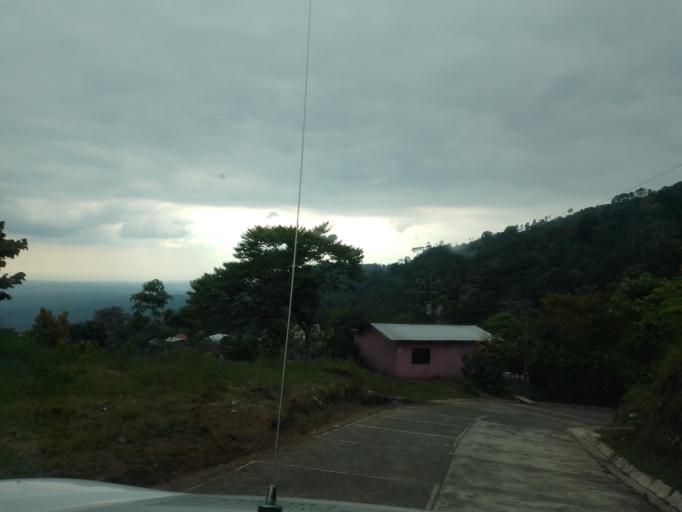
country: MX
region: Chiapas
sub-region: Union Juarez
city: Santo Domingo
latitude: 15.0560
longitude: -92.1118
